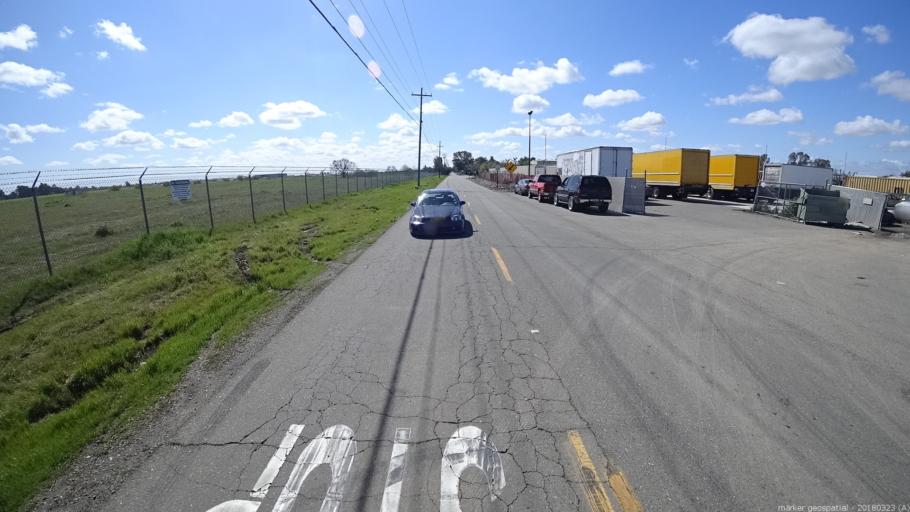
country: US
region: California
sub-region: Sacramento County
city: North Highlands
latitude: 38.6891
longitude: -121.4060
